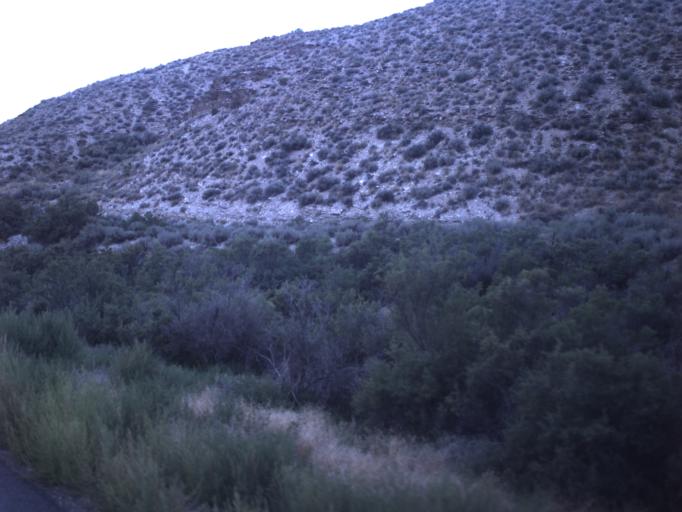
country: US
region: Utah
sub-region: Duchesne County
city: Duchesne
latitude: 40.1096
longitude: -110.4585
